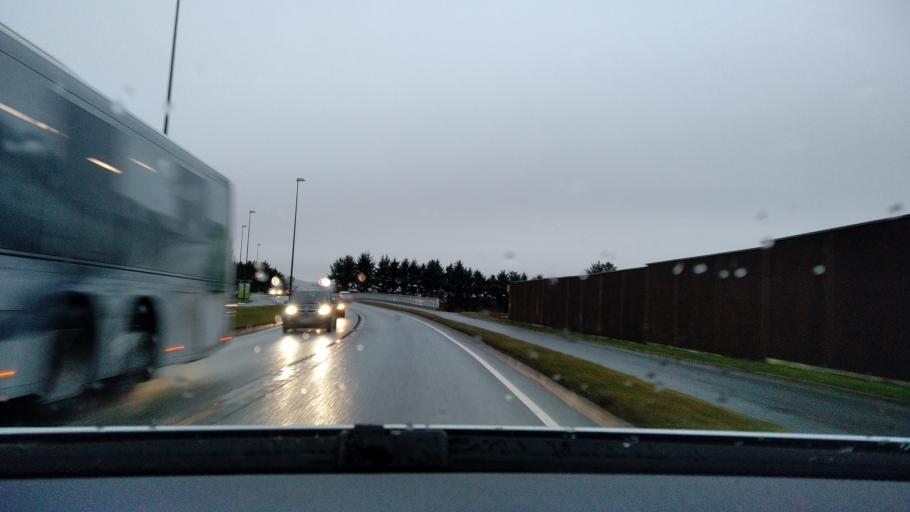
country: NO
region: Rogaland
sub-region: Randaberg
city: Randaberg
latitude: 58.9543
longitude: 5.6385
